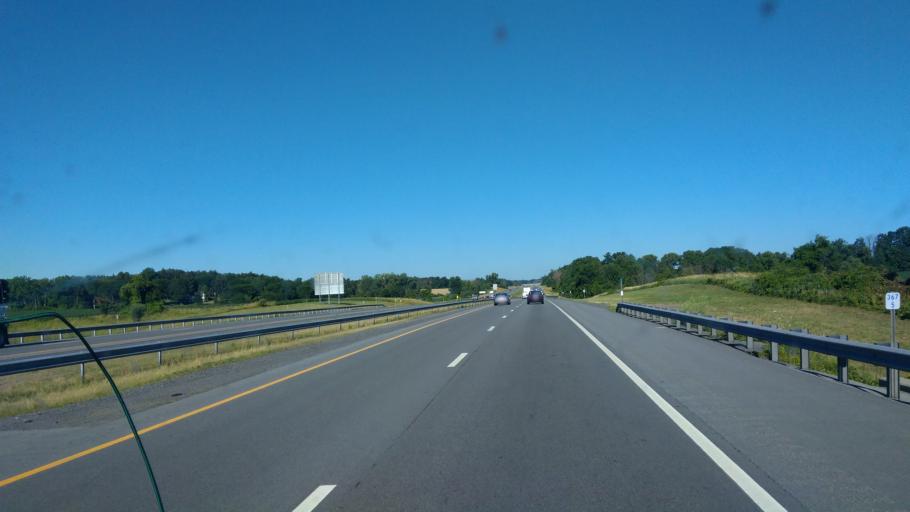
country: US
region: New York
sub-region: Monroe County
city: Scottsville
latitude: 43.0454
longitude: -77.7499
